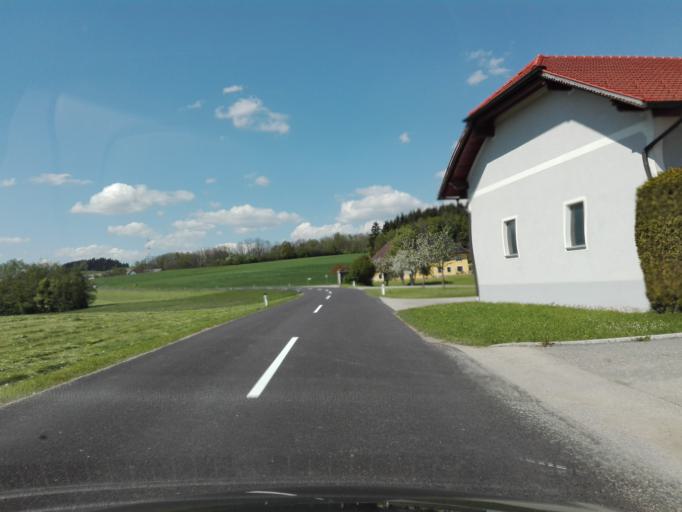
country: AT
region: Upper Austria
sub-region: Politischer Bezirk Urfahr-Umgebung
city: Feldkirchen an der Donau
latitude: 48.3551
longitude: 13.9403
